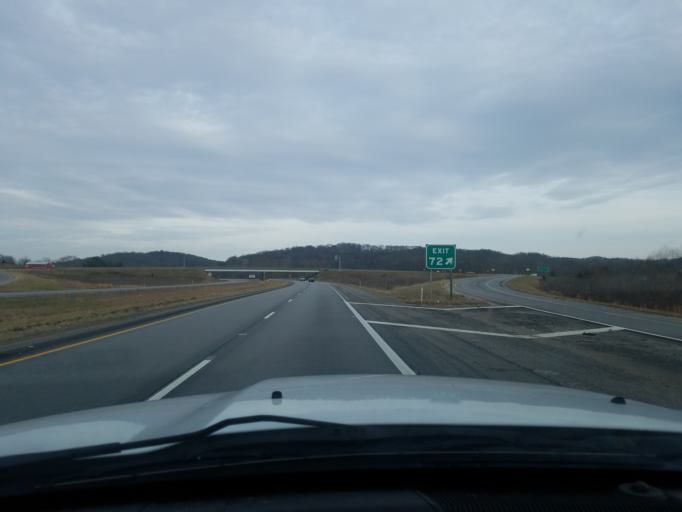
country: US
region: Indiana
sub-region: Dubois County
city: Ferdinand
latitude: 38.2241
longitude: -86.7034
